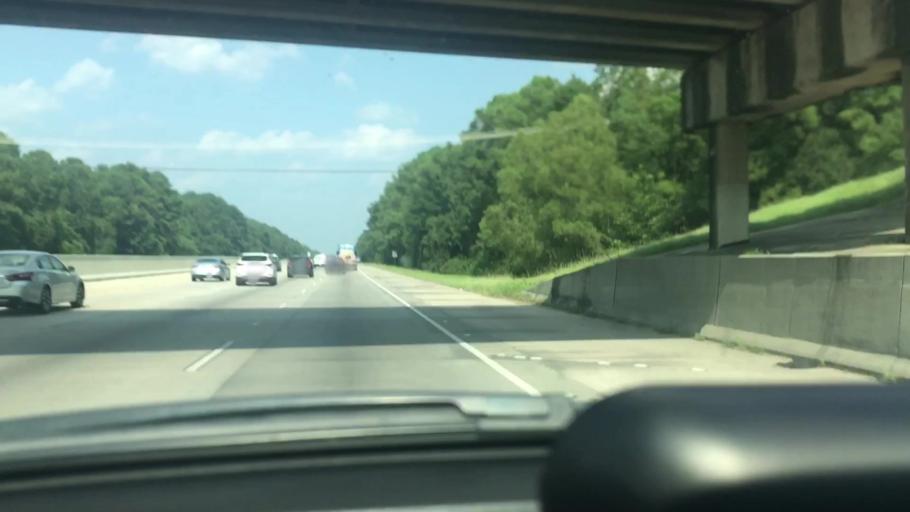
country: US
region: Louisiana
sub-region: Livingston Parish
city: Denham Springs
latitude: 30.4573
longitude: -90.9469
